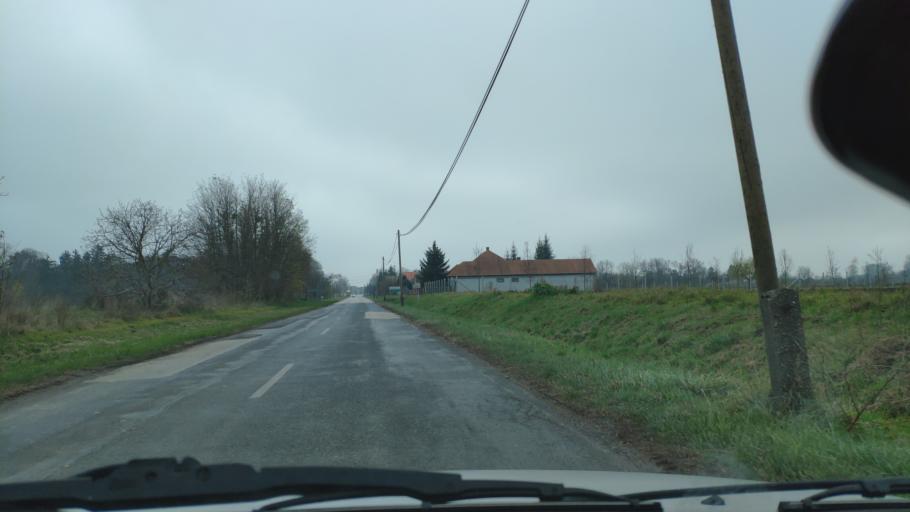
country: HU
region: Somogy
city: Balatonbereny
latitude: 46.6776
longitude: 17.2869
